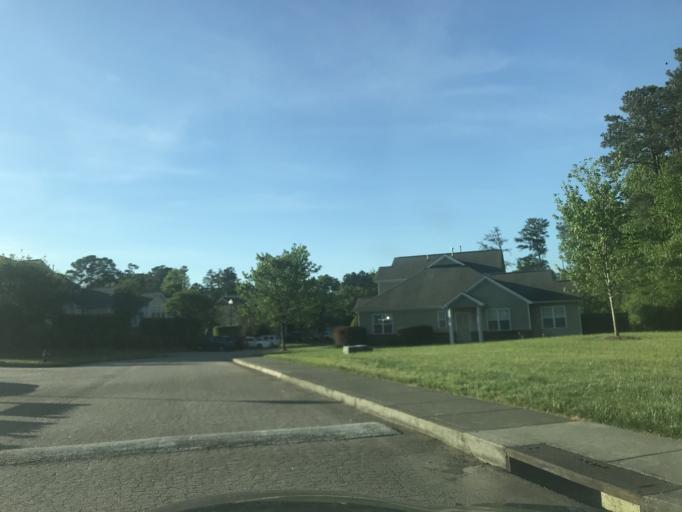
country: US
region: North Carolina
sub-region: Wake County
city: Raleigh
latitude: 35.8204
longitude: -78.5664
